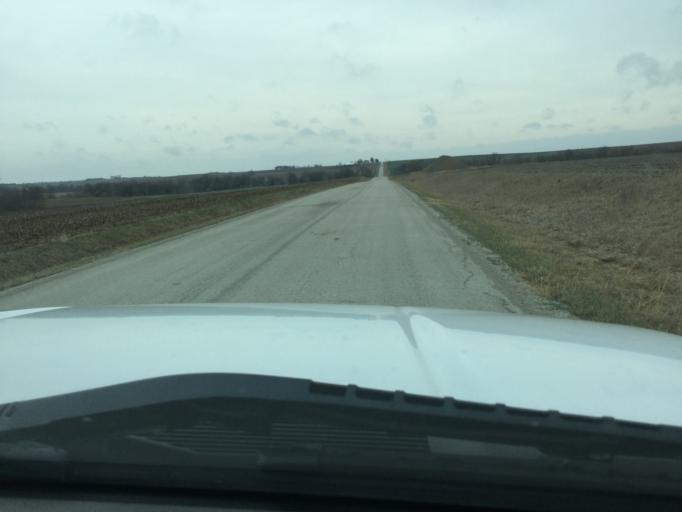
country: US
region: Kansas
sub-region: Nemaha County
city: Sabetha
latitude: 39.8486
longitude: -95.7142
